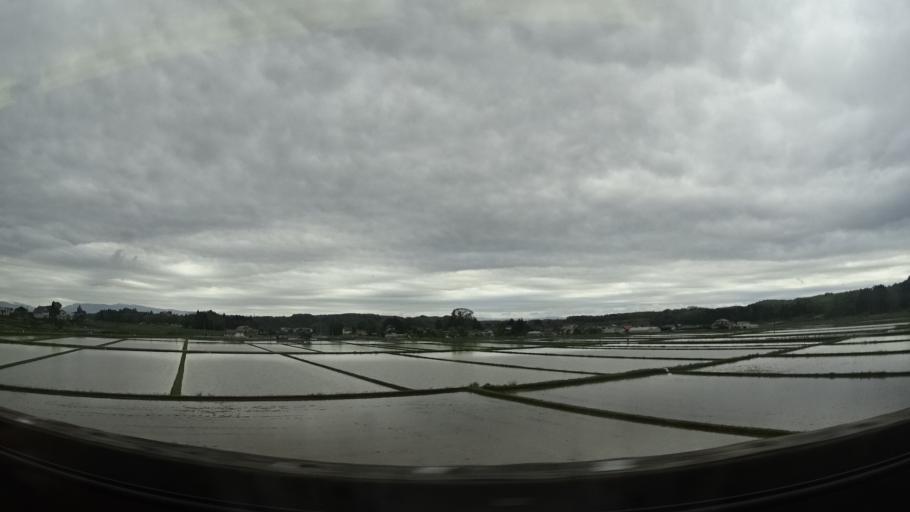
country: JP
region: Fukushima
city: Sukagawa
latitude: 37.2410
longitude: 140.2951
